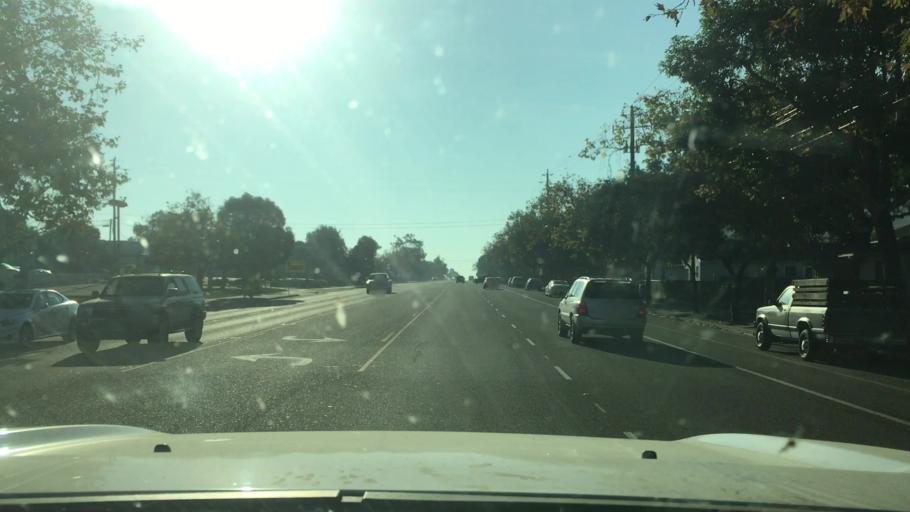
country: US
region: California
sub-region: San Luis Obispo County
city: San Luis Obispo
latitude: 35.2665
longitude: -120.6540
